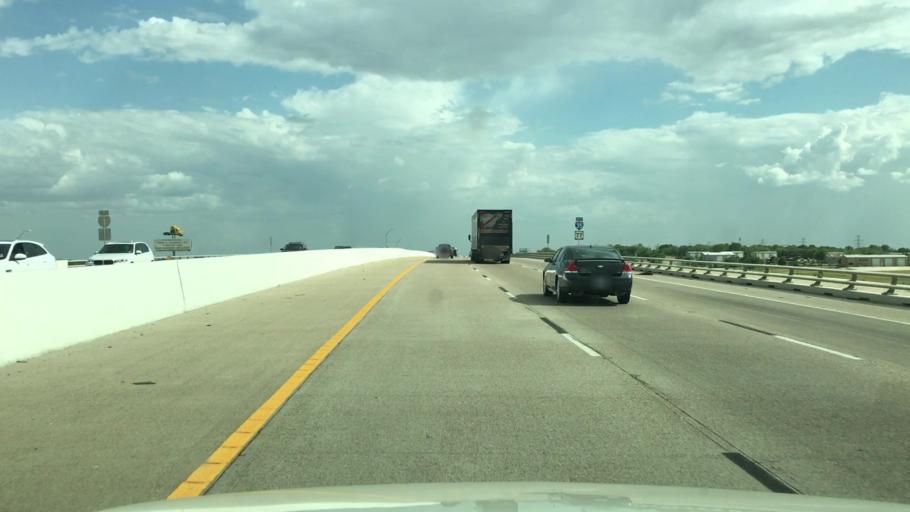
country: US
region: Texas
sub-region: McLennan County
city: Northcrest
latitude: 31.6897
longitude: -97.1001
